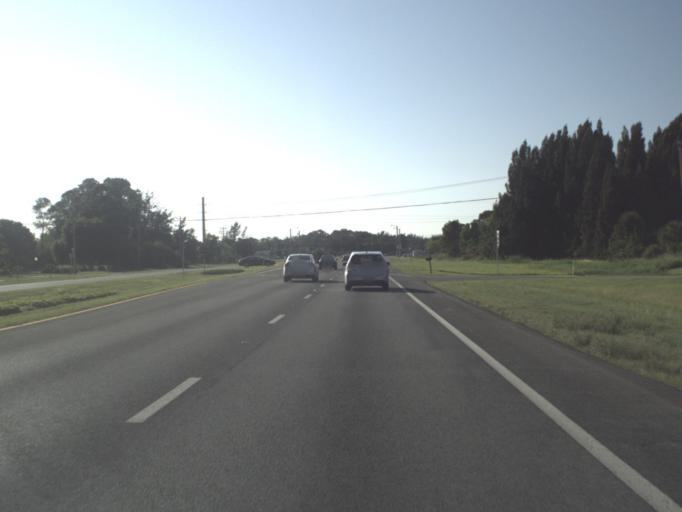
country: US
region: Florida
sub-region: Lee County
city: Suncoast Estates
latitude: 26.7291
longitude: -81.9087
